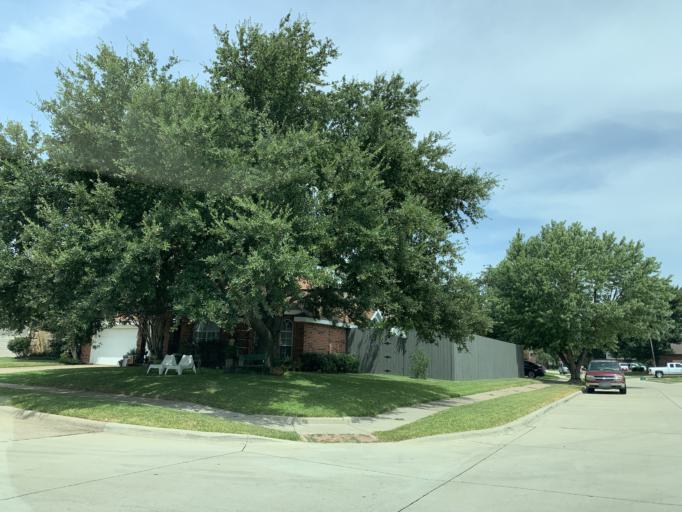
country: US
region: Texas
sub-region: Dallas County
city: Cedar Hill
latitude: 32.6567
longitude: -97.0081
